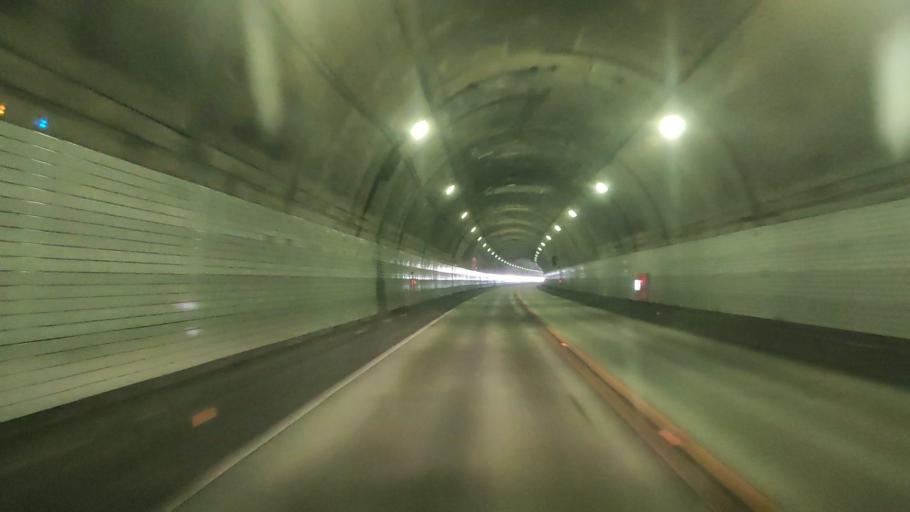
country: JP
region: Fukuoka
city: Maebaru-chuo
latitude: 33.4681
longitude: 130.2805
